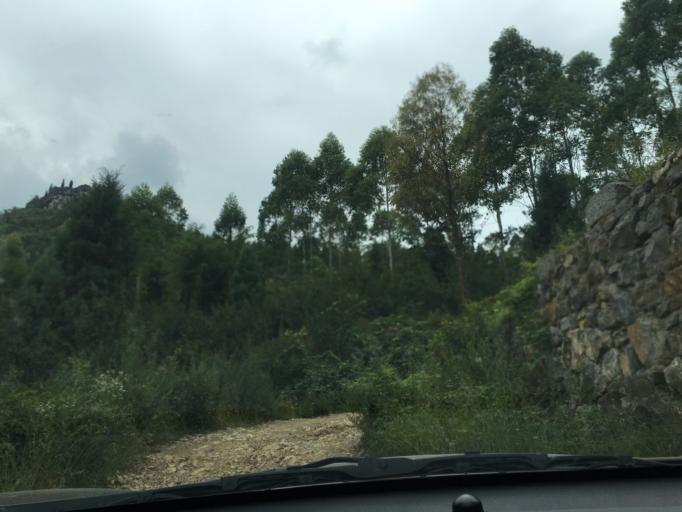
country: CN
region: Guangxi Zhuangzu Zizhiqu
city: Xinzhou
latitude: 25.3802
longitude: 105.6365
